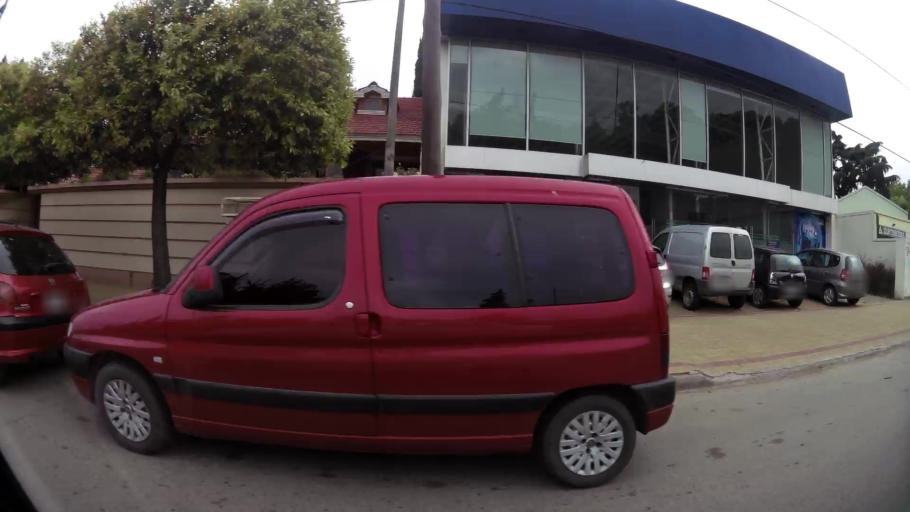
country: AR
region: Buenos Aires
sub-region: Partido de La Plata
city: La Plata
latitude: -34.9470
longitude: -57.9950
